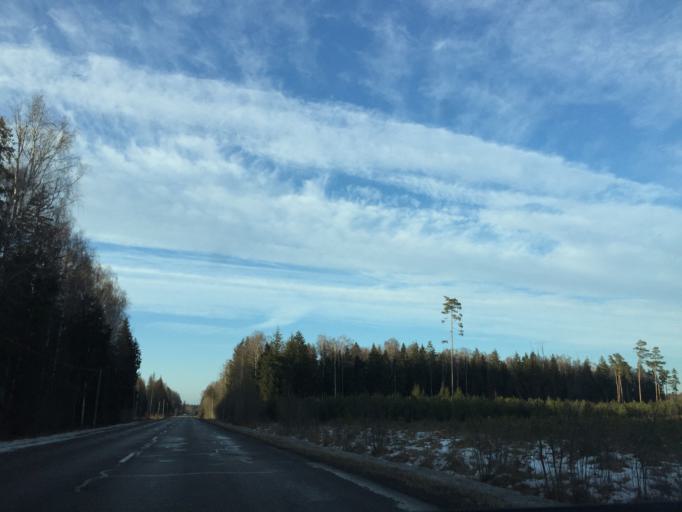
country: LV
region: Kekava
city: Balozi
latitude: 56.8037
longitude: 24.0722
